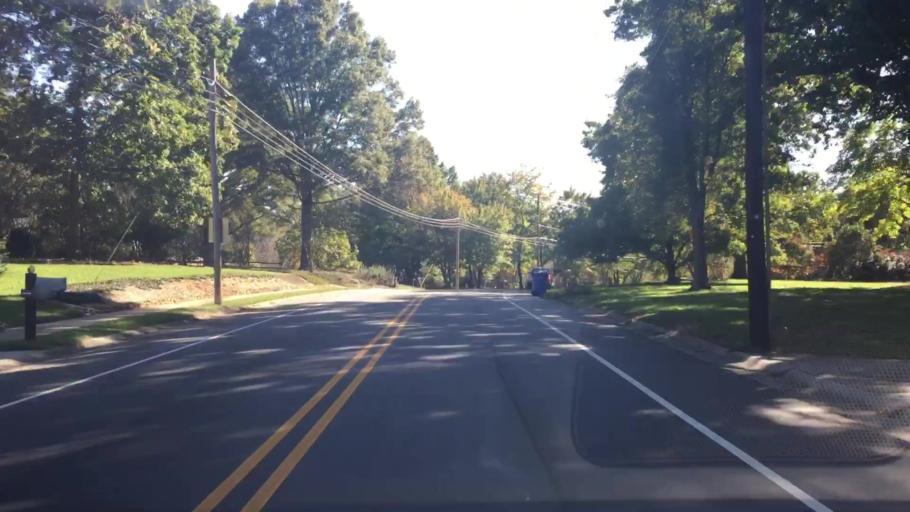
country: US
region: North Carolina
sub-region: Iredell County
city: Mooresville
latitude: 35.5696
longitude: -80.8016
